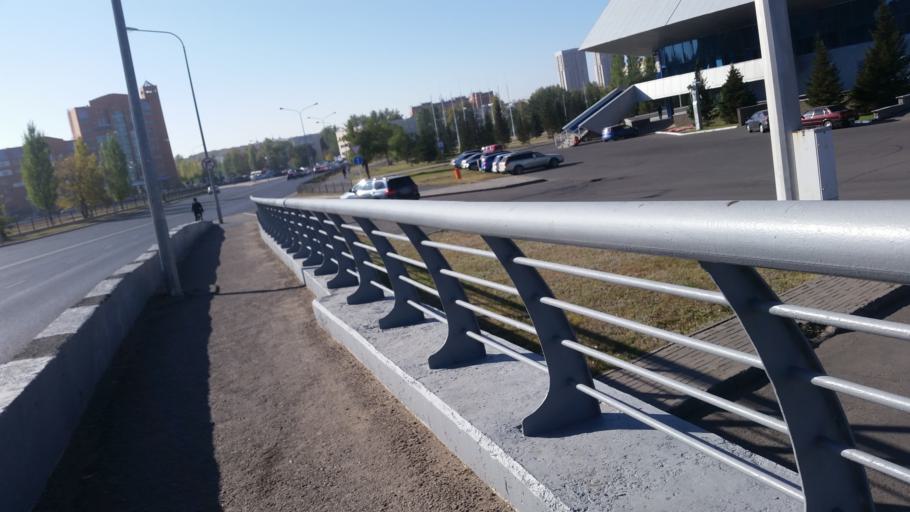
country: KZ
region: Astana Qalasy
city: Astana
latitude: 51.1564
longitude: 71.4667
